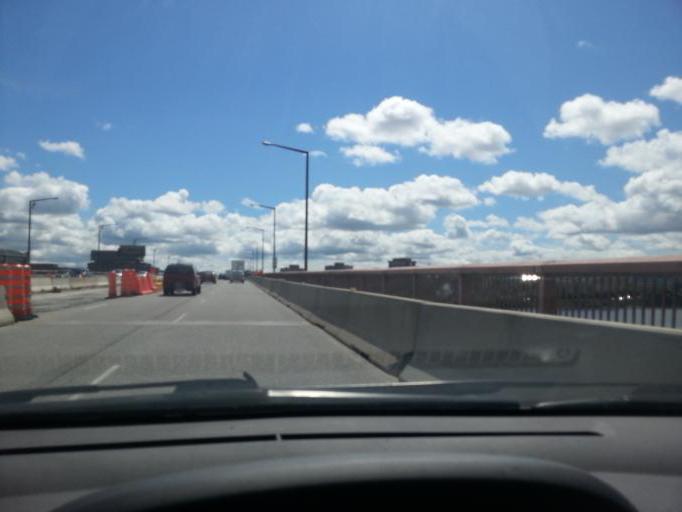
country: CA
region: Ontario
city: Ottawa
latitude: 45.4376
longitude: -75.7056
